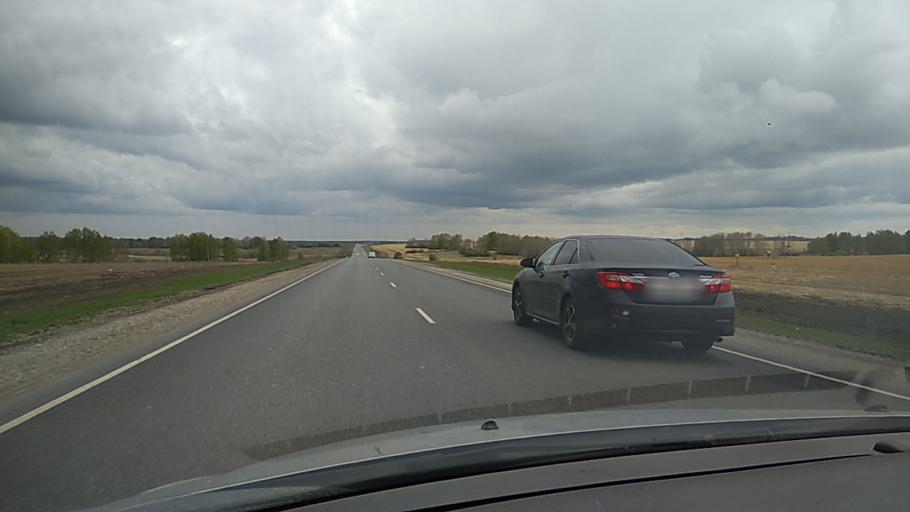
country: RU
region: Kurgan
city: Dalmatovo
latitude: 56.2888
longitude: 62.7688
